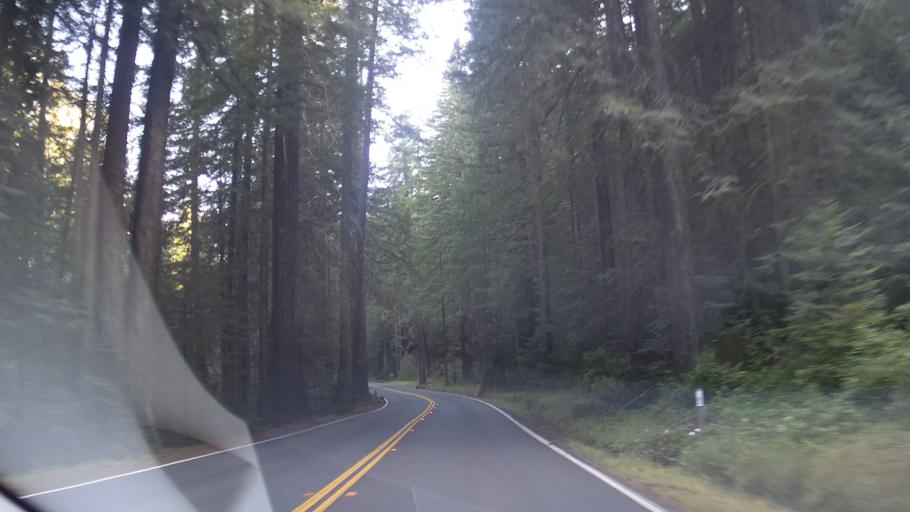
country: US
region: California
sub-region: Mendocino County
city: Brooktrails
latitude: 39.3510
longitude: -123.5621
